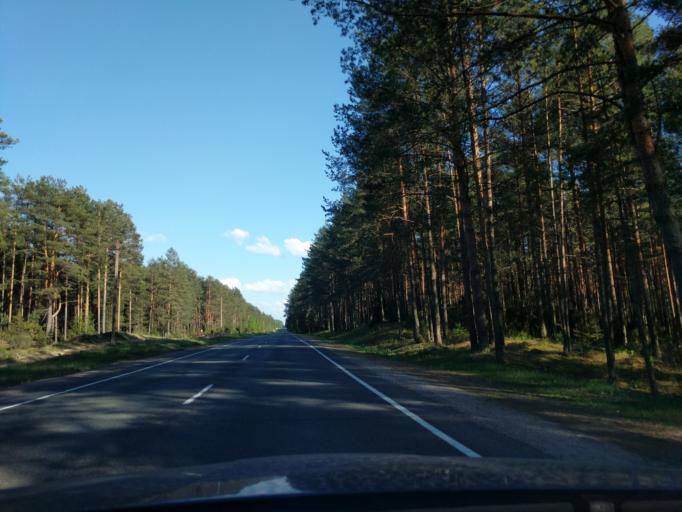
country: BY
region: Minsk
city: Myadzyel
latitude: 54.8227
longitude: 26.9537
